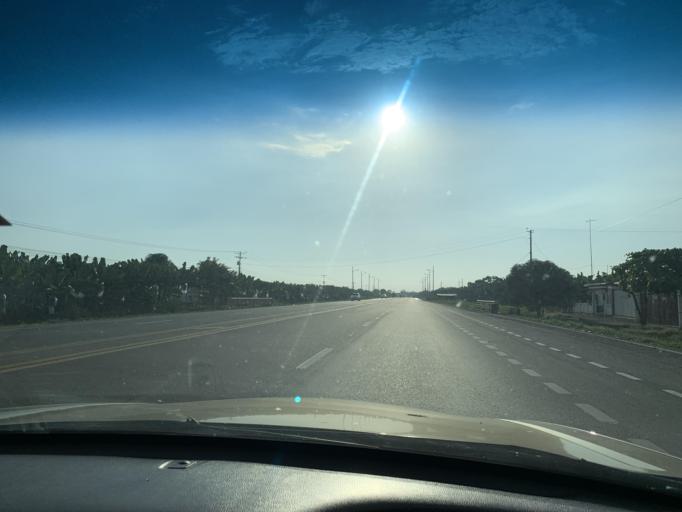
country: EC
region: Guayas
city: Naranjito
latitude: -2.2547
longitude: -79.6162
